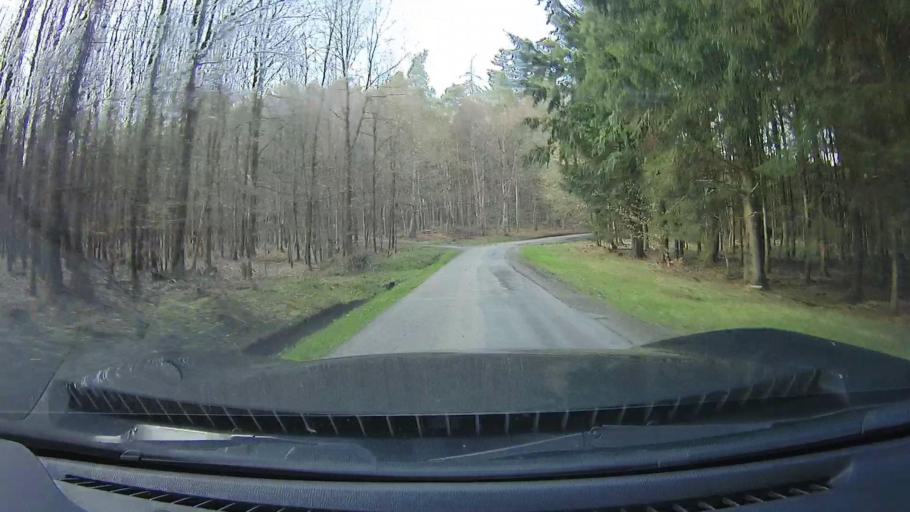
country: DE
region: Bavaria
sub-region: Regierungsbezirk Unterfranken
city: Weilbach
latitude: 49.6081
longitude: 9.2791
